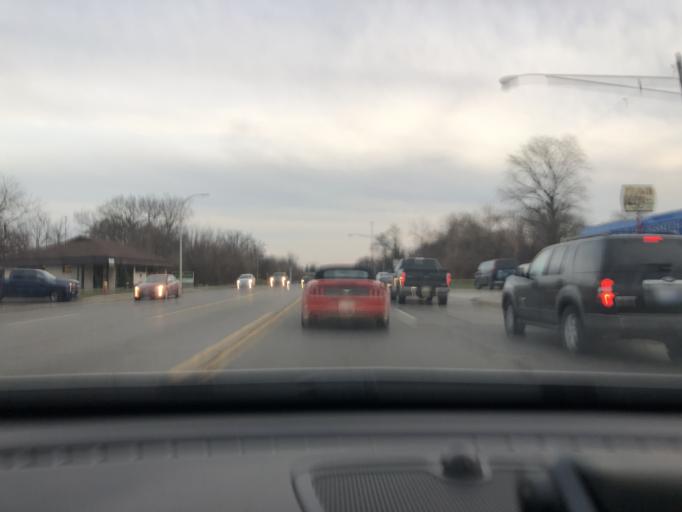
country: US
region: Michigan
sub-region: Wayne County
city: Allen Park
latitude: 42.2693
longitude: -83.2319
